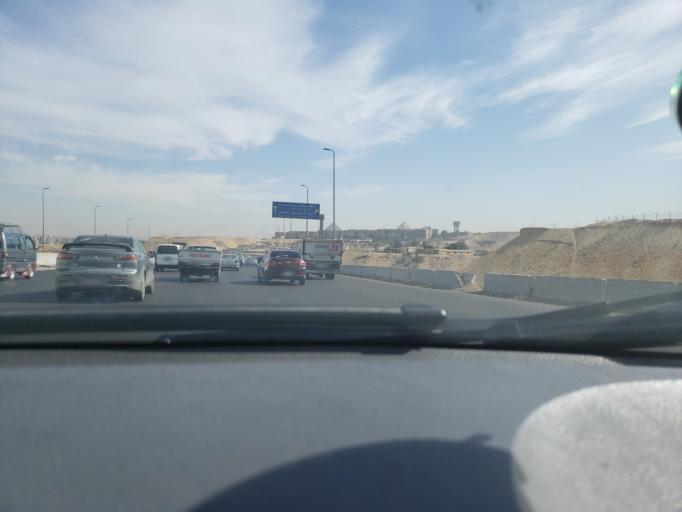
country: EG
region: Al Jizah
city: Al Jizah
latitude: 29.9978
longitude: 31.1029
